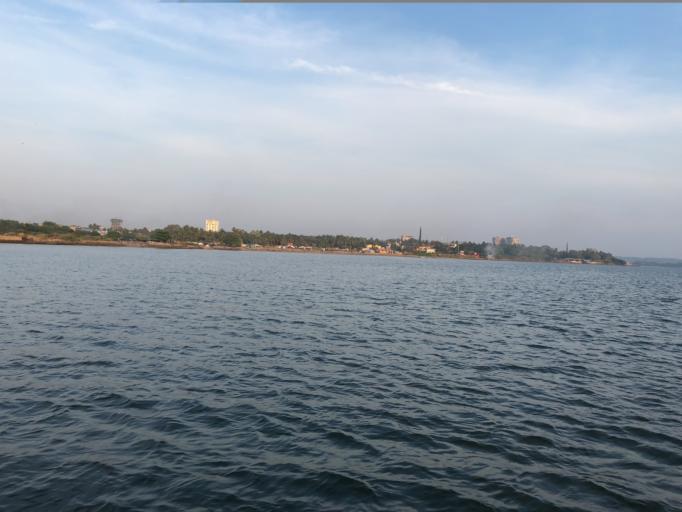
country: IN
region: Karnataka
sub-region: Dakshina Kannada
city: Ullal
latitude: 12.8482
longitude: 74.8314
